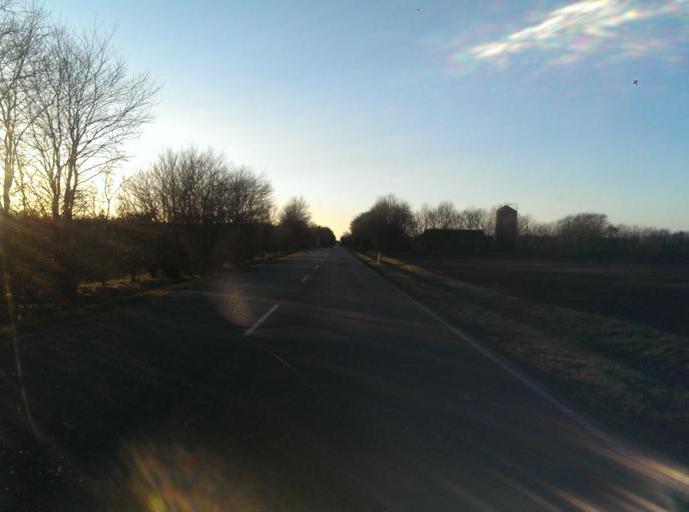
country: DK
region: South Denmark
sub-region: Esbjerg Kommune
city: Tjaereborg
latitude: 55.4933
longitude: 8.5831
